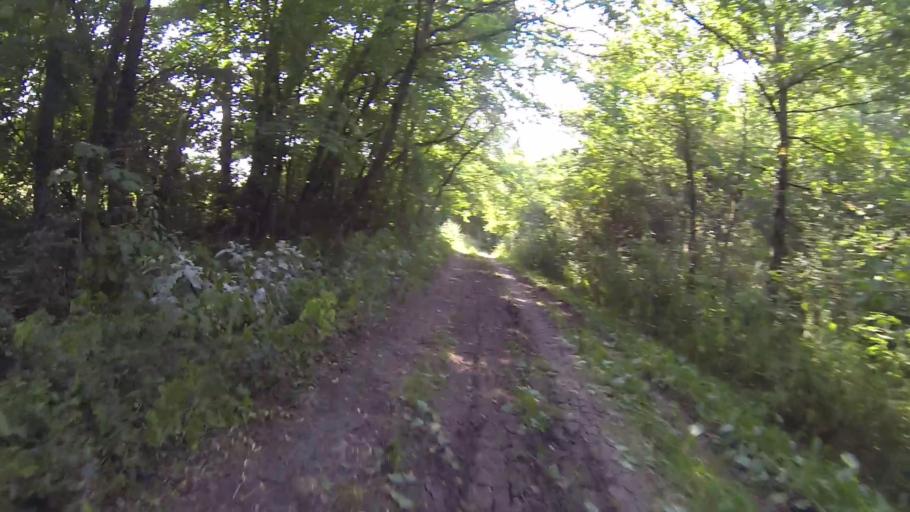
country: DE
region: Baden-Wuerttemberg
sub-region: Tuebingen Region
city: Dornstadt
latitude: 48.4424
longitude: 9.9017
